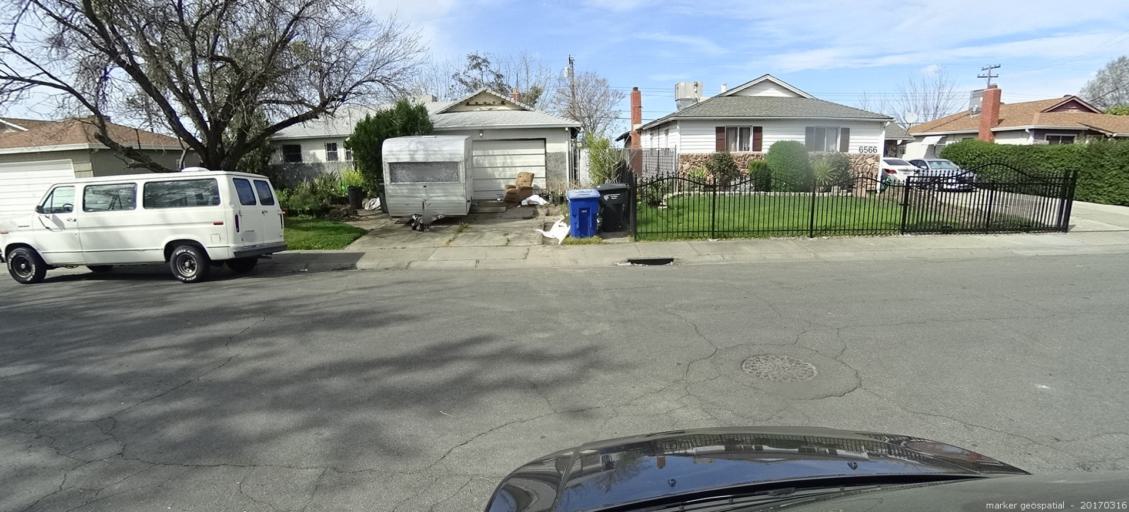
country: US
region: California
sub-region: Sacramento County
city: Parkway
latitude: 38.5076
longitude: -121.4917
